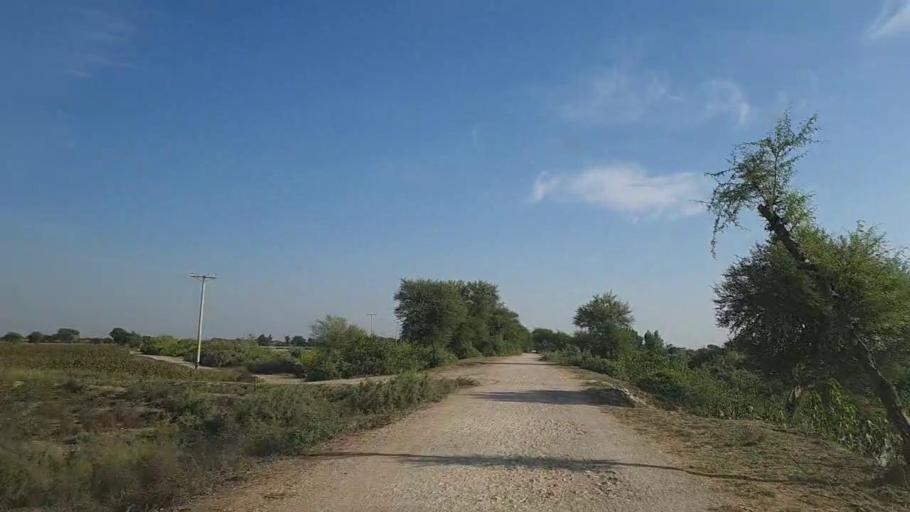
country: PK
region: Sindh
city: Bulri
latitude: 24.7805
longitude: 68.3540
